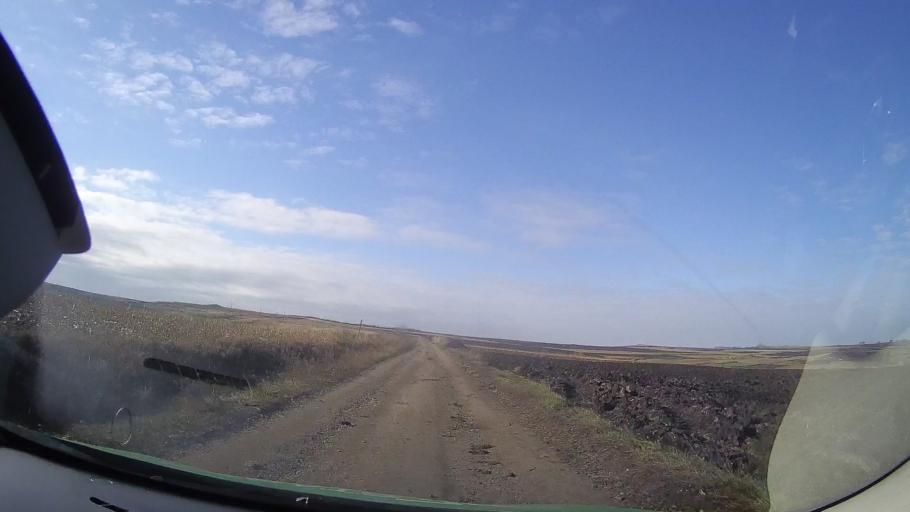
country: RO
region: Mures
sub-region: Comuna Saulia
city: Saulia
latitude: 46.5984
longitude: 24.2287
